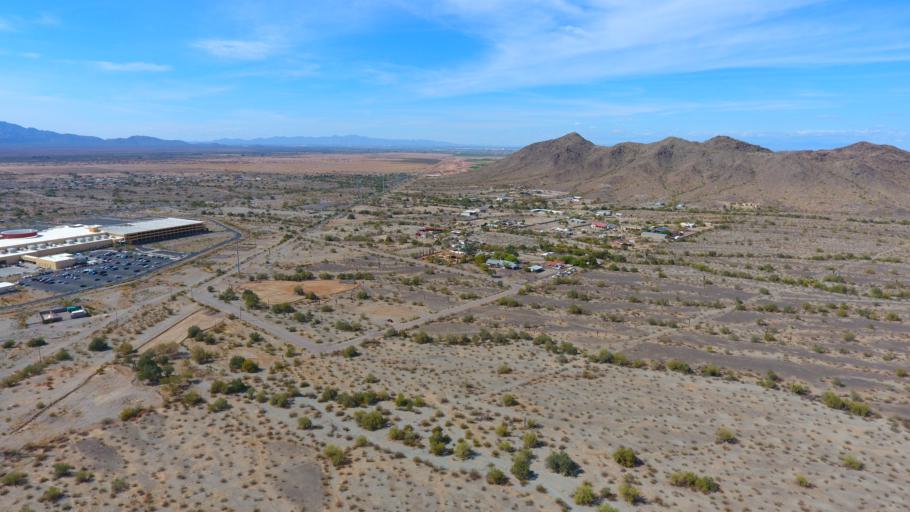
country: US
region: Arizona
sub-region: Maricopa County
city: Laveen
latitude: 33.3088
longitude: -112.1494
